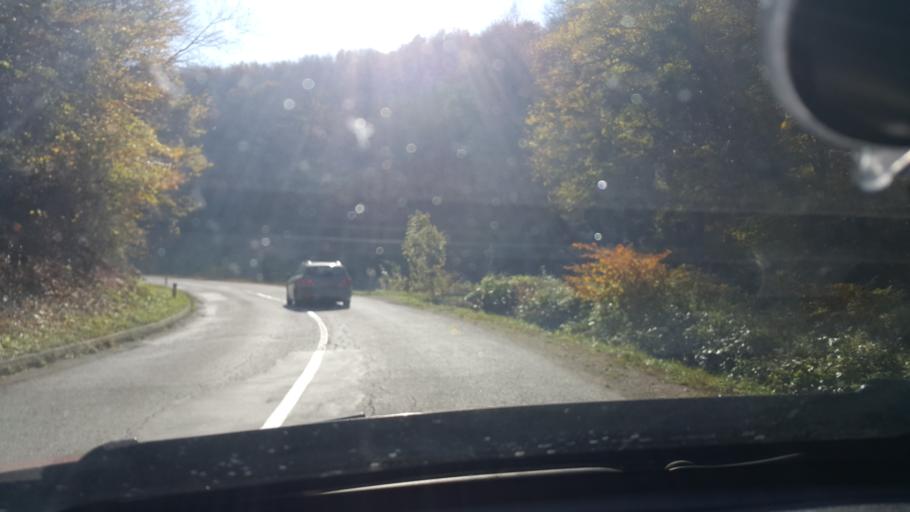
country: SI
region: Bistrica ob Sotli
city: Bistrica ob Sotli
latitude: 46.0390
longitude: 15.6870
